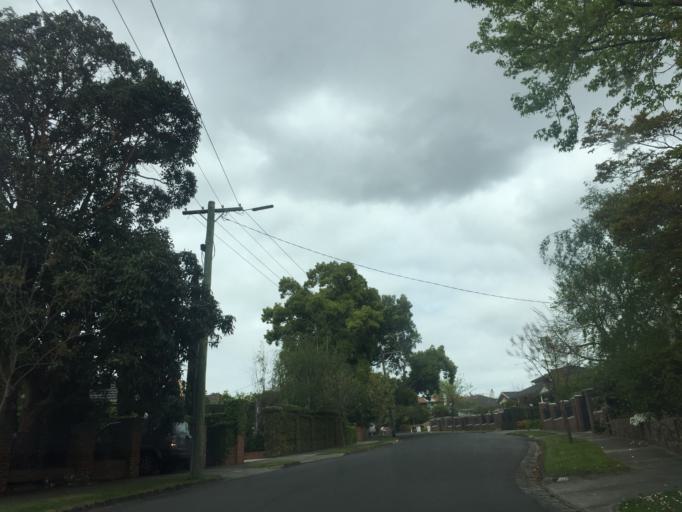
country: AU
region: Victoria
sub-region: Boroondara
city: Kew East
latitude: -37.8059
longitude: 145.0471
